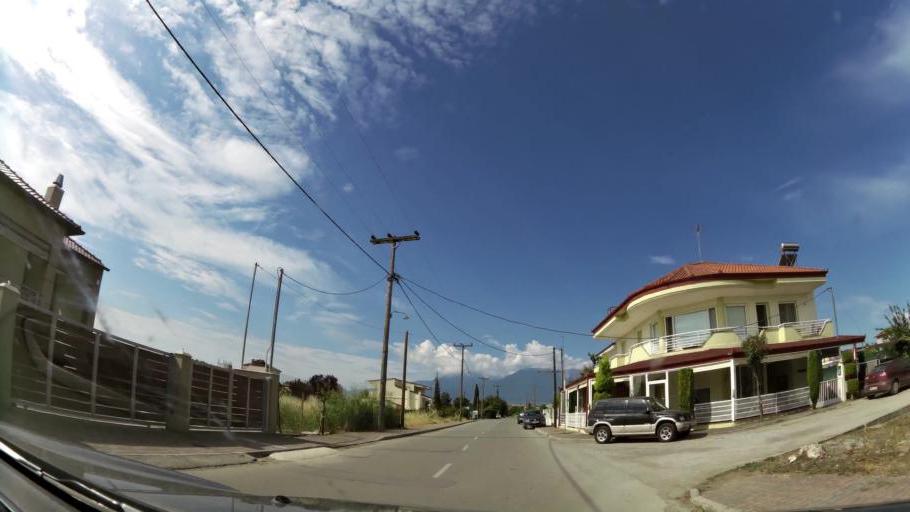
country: GR
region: Central Macedonia
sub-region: Nomos Pierias
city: Katerini
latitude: 40.2814
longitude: 22.5136
